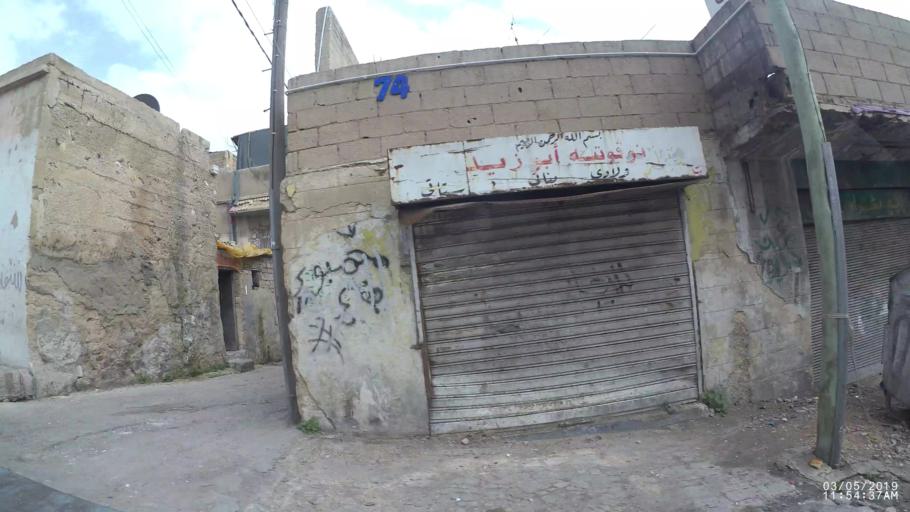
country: JO
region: Amman
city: Amman
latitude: 31.9658
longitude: 35.9290
